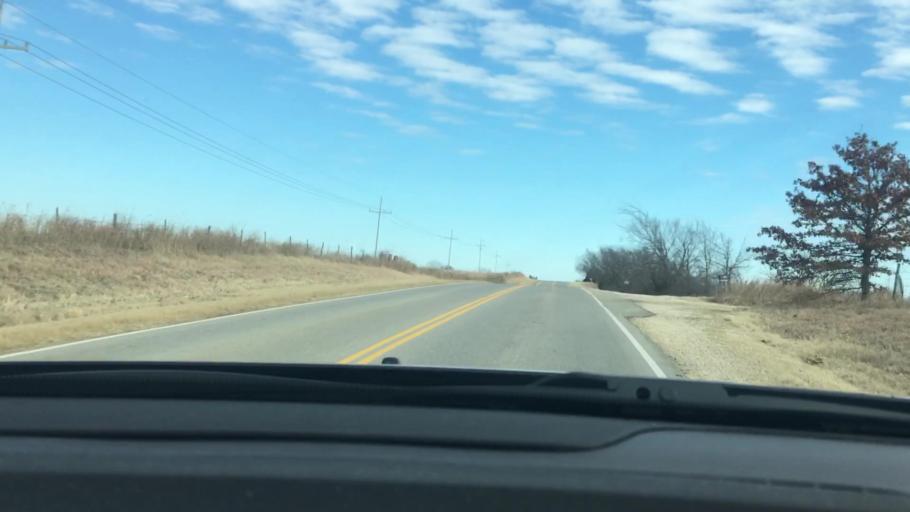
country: US
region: Oklahoma
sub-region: Garvin County
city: Stratford
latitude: 34.7968
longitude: -96.8343
